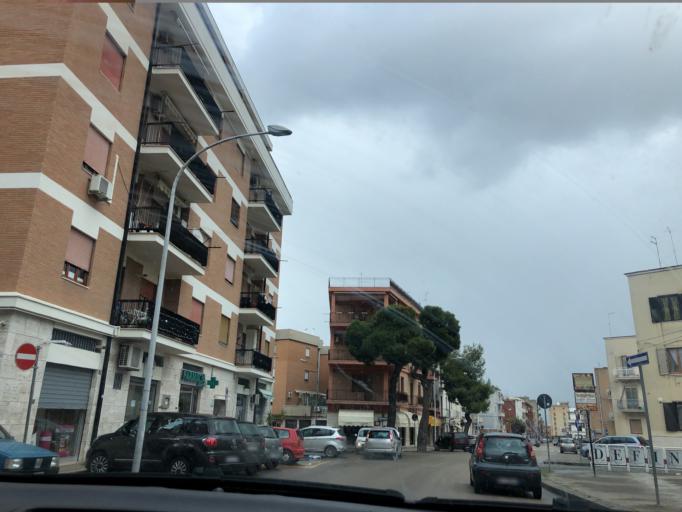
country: IT
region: Apulia
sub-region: Provincia di Foggia
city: Lucera
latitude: 41.5118
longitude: 15.3338
